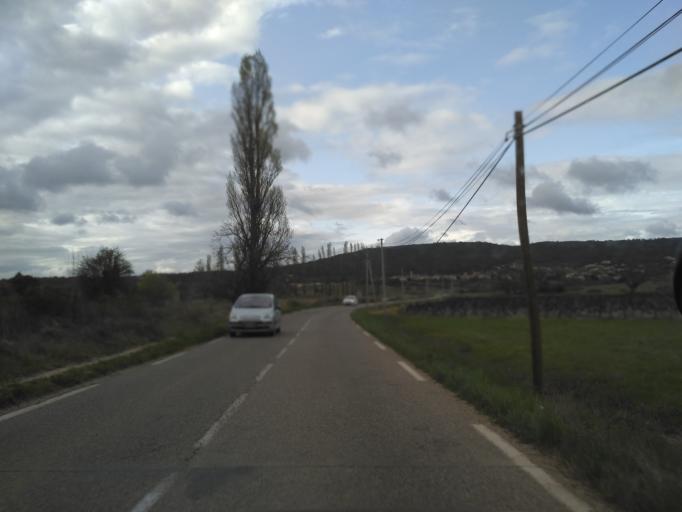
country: FR
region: Provence-Alpes-Cote d'Azur
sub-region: Departement du Var
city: Barjols
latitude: 43.5797
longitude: 6.0154
